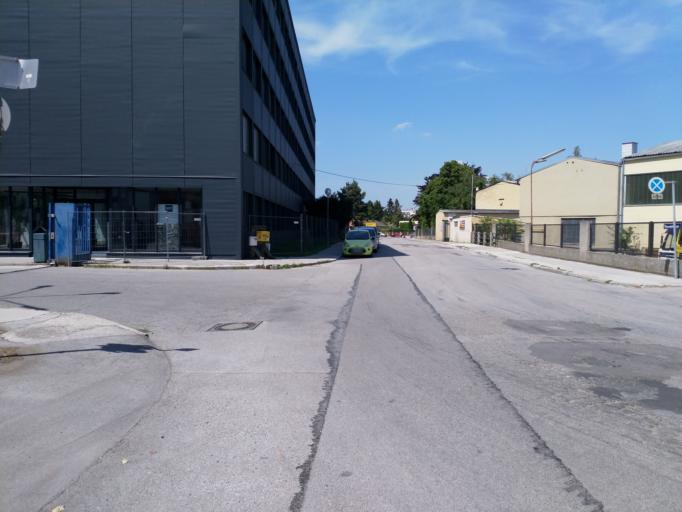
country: AT
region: Lower Austria
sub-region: Politischer Bezirk Baden
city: Traiskirchen
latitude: 48.0116
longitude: 16.2916
